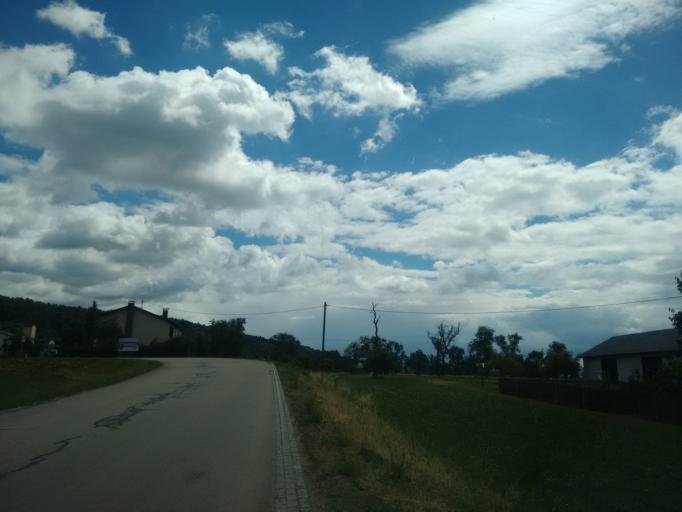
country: AT
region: Upper Austria
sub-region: Politischer Bezirk Urfahr-Umgebung
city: Feldkirchen an der Donau
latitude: 48.3614
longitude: 14.0292
